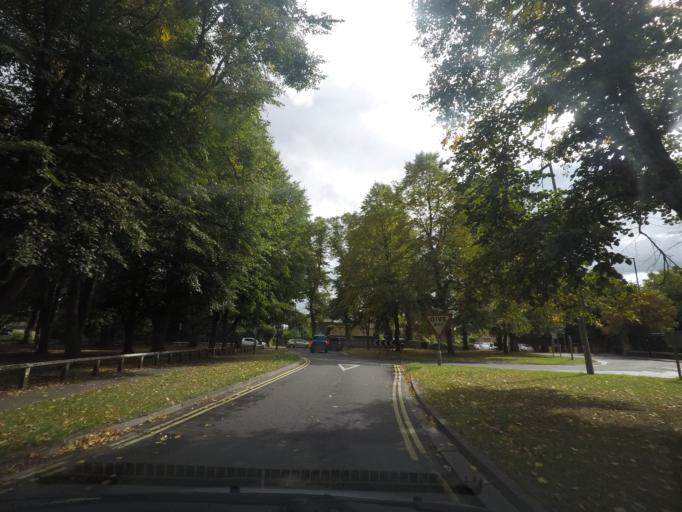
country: GB
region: England
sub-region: City of York
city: Heslington
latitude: 53.9465
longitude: -1.0461
